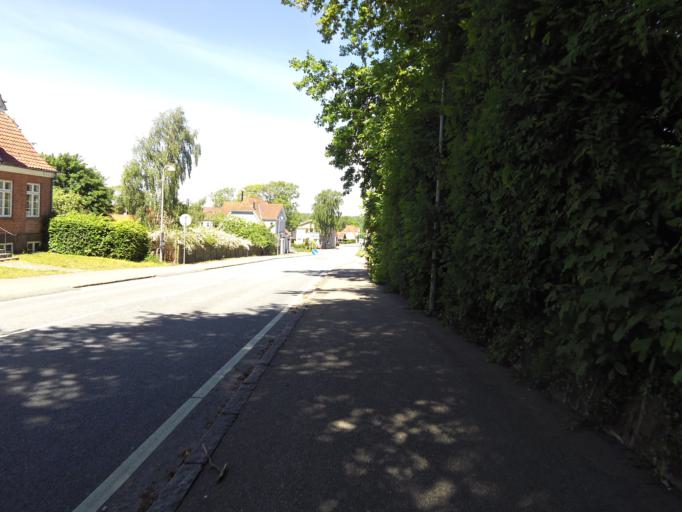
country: DK
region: South Denmark
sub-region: Haderslev Kommune
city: Gram
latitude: 55.2931
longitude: 9.0539
